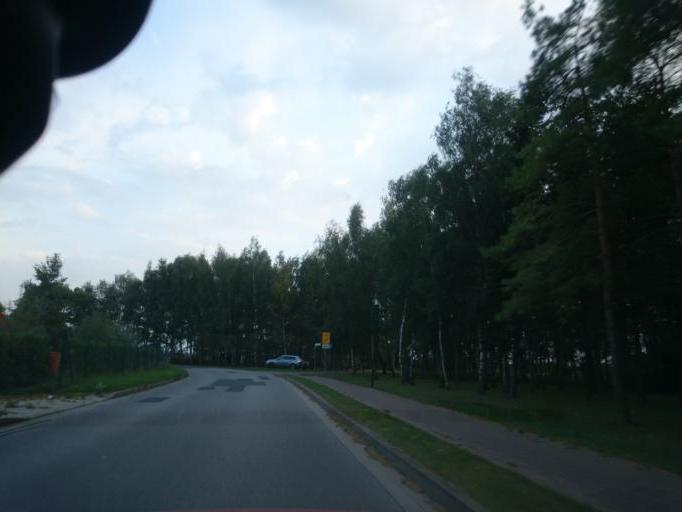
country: DE
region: Mecklenburg-Vorpommern
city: Saal
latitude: 54.3072
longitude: 12.5011
